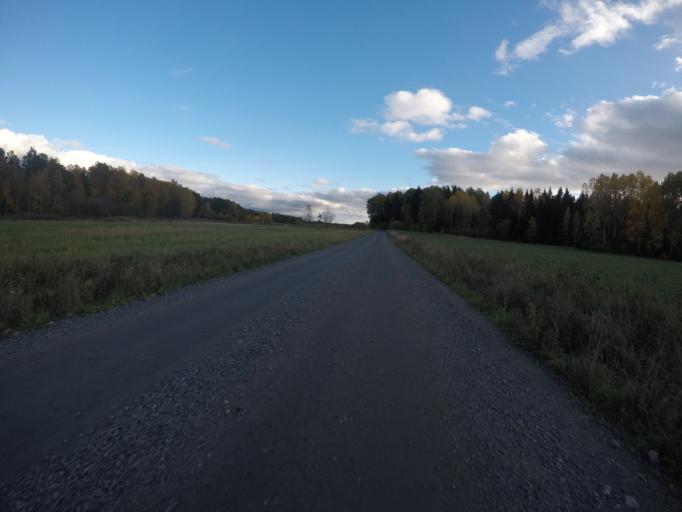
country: SE
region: Vaestmanland
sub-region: Arboga Kommun
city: Tyringe
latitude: 59.3095
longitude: 15.9761
